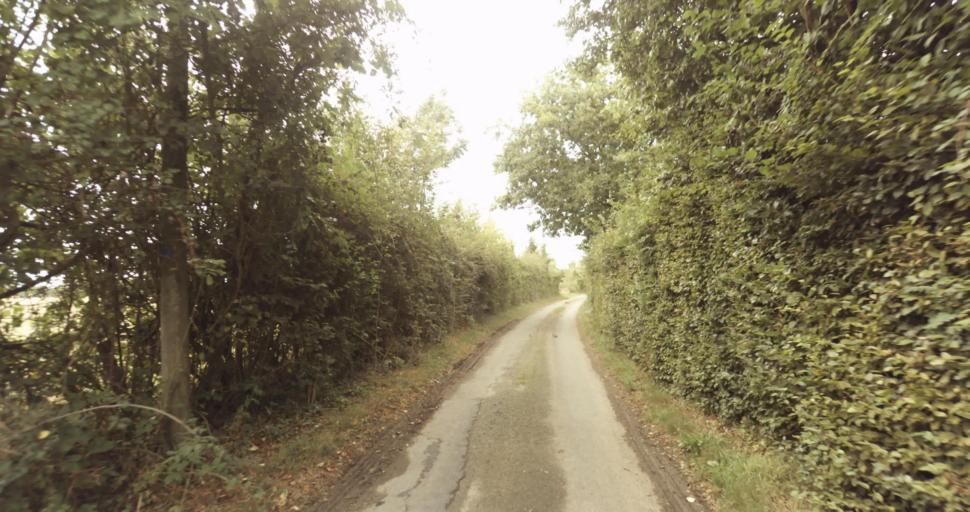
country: FR
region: Lower Normandy
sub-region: Departement de l'Orne
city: Gace
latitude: 48.8340
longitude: 0.3015
